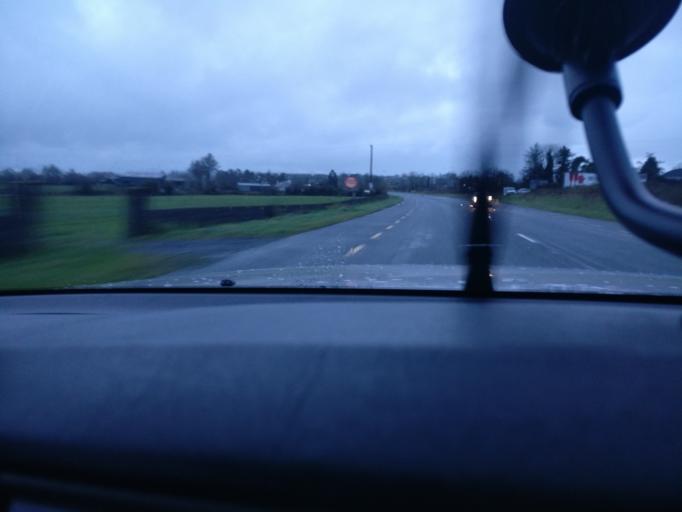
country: IE
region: Connaught
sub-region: County Galway
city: Ballinasloe
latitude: 53.2706
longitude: -8.3958
